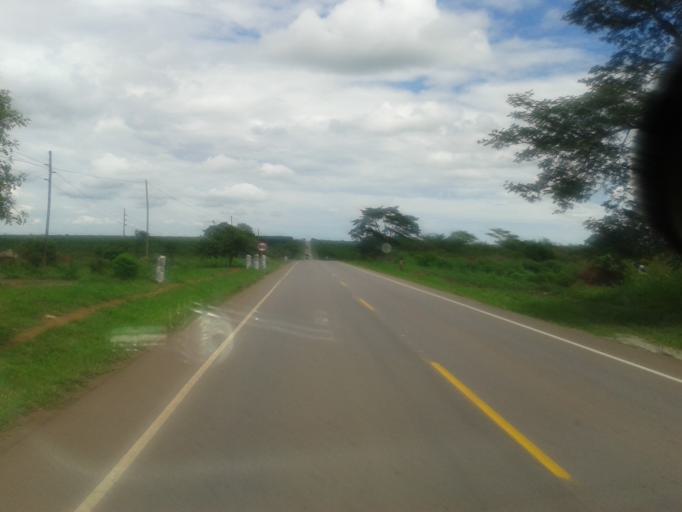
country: UG
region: Western Region
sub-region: Kiryandongo District
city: Masindi Port
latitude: 1.7640
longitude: 32.0201
